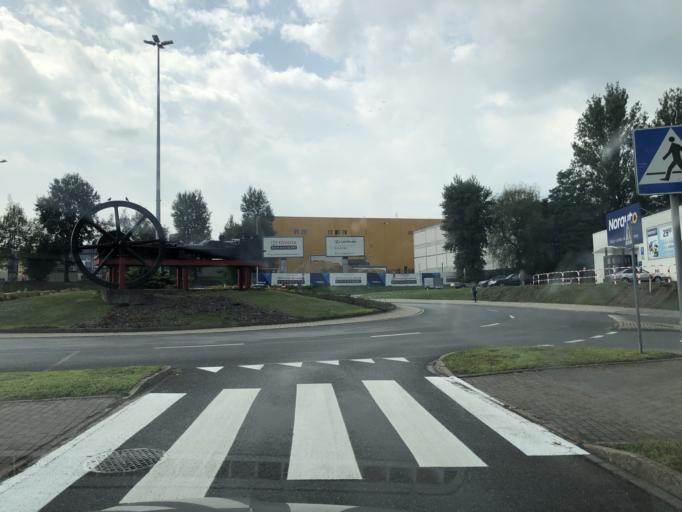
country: PL
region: Lesser Poland Voivodeship
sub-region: Krakow
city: Krakow
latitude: 50.0134
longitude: 19.9303
